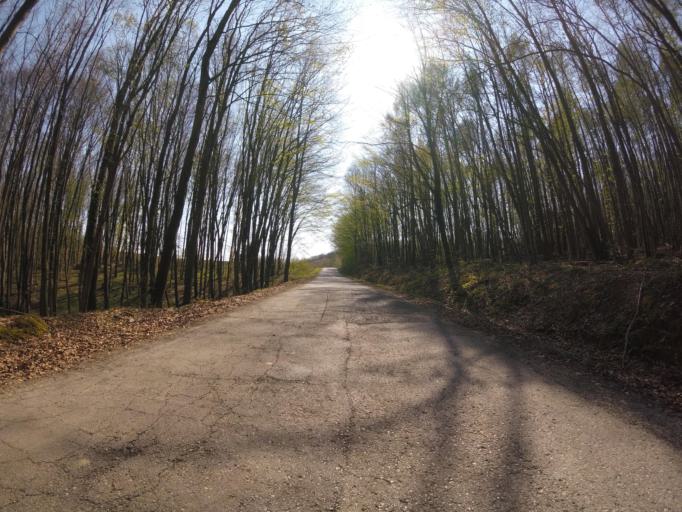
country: HR
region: Grad Zagreb
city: Strmec
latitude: 45.5807
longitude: 15.9203
